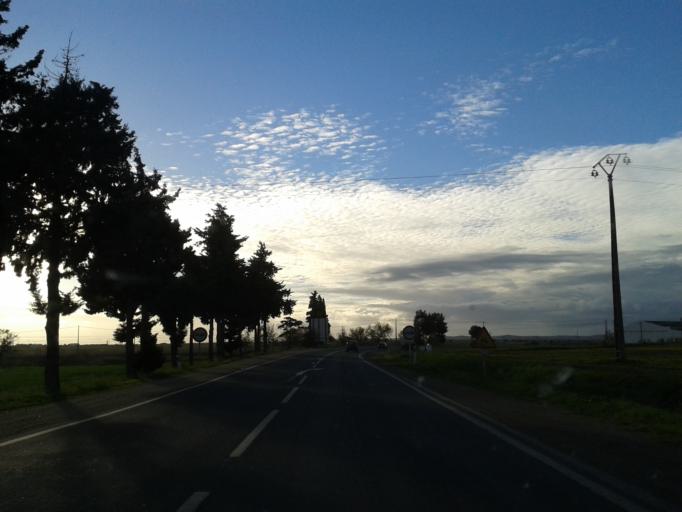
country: PT
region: Beja
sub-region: Beja
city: Beja
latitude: 38.0254
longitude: -7.8775
